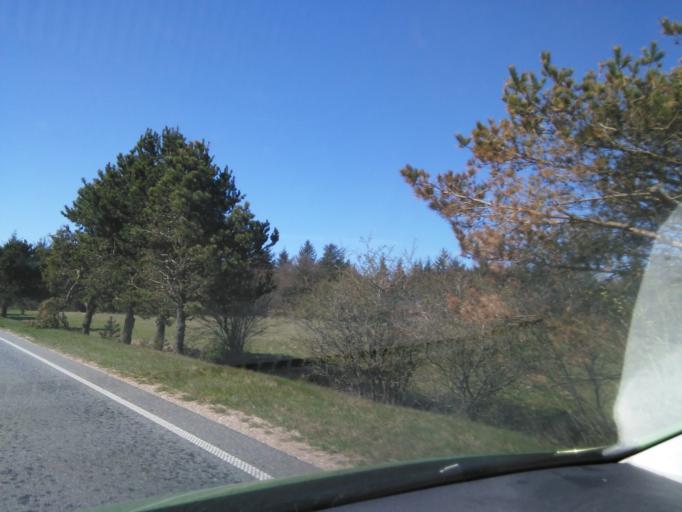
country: DK
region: South Denmark
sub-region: Varde Kommune
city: Oksbol
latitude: 55.6152
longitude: 8.2379
